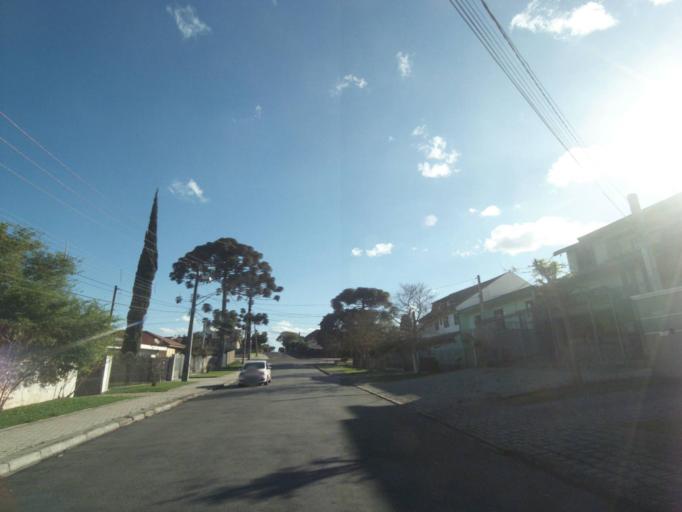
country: BR
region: Parana
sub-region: Curitiba
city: Curitiba
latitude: -25.3875
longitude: -49.2458
